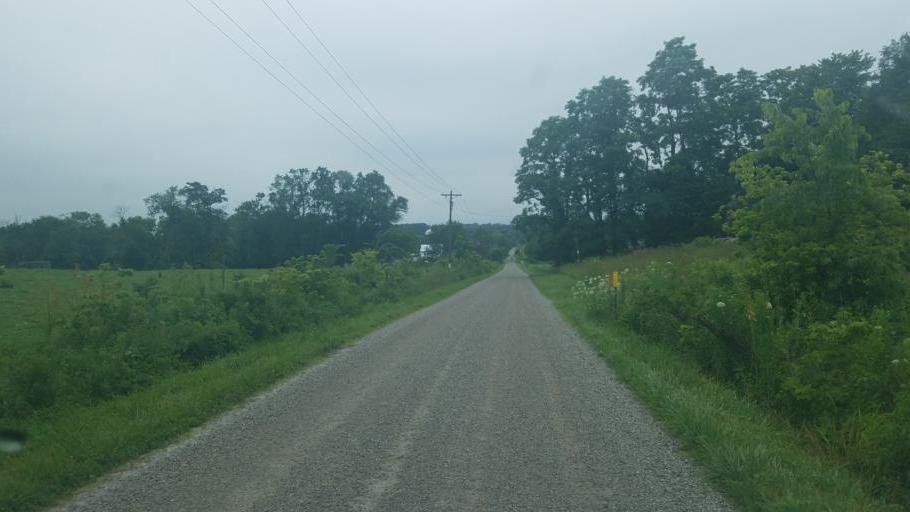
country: US
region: Ohio
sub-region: Knox County
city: Fredericktown
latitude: 40.5080
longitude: -82.6442
